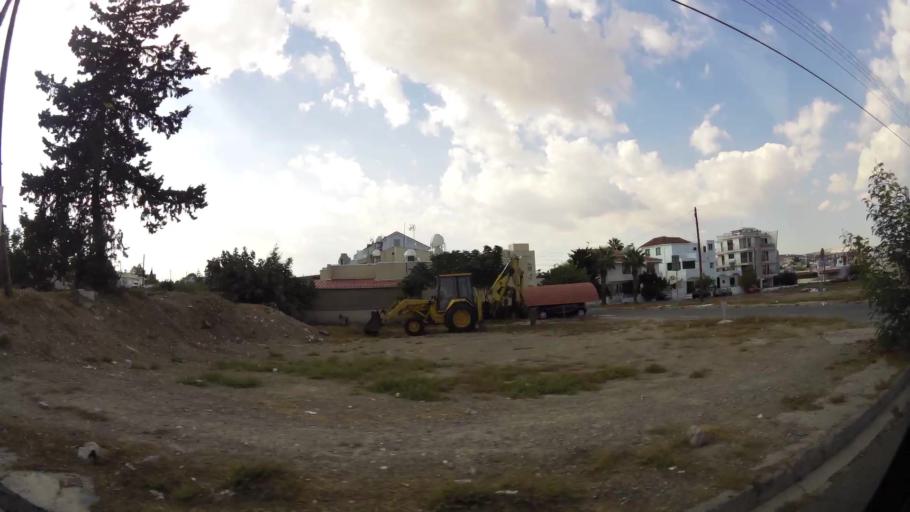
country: CY
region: Larnaka
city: Larnaca
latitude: 34.9092
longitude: 33.5942
